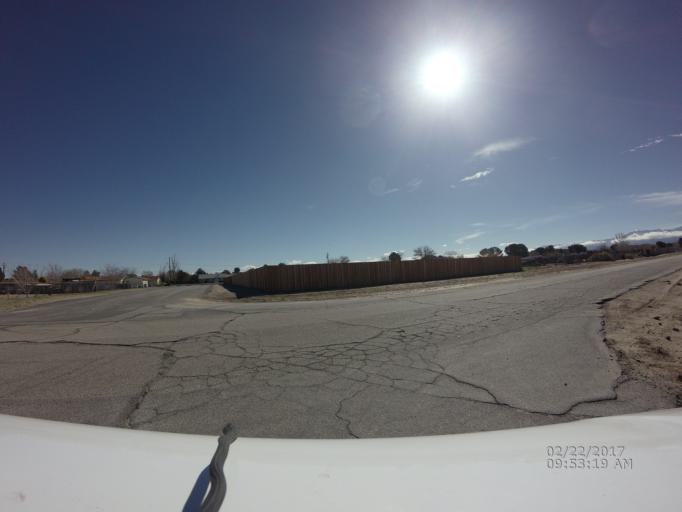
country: US
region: California
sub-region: Los Angeles County
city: Lake Los Angeles
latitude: 34.6201
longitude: -117.8359
